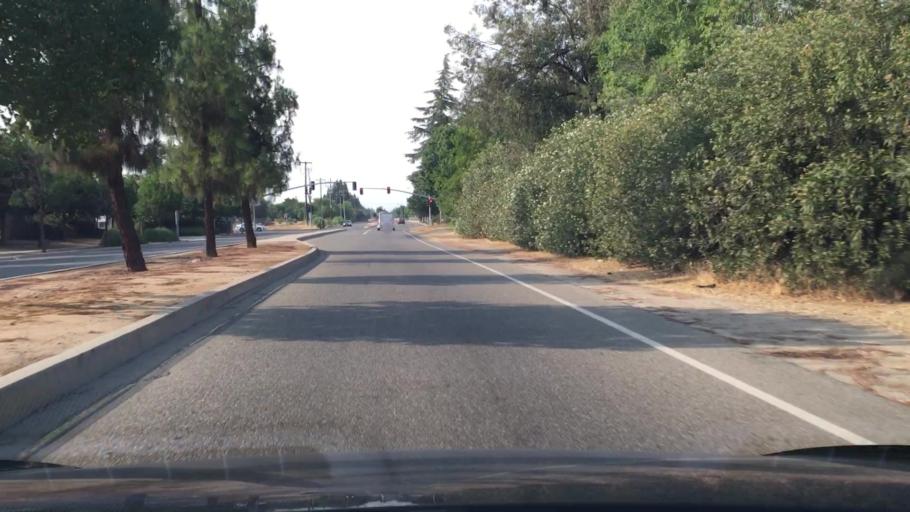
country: US
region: California
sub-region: Fresno County
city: Clovis
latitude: 36.8435
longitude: -119.7387
